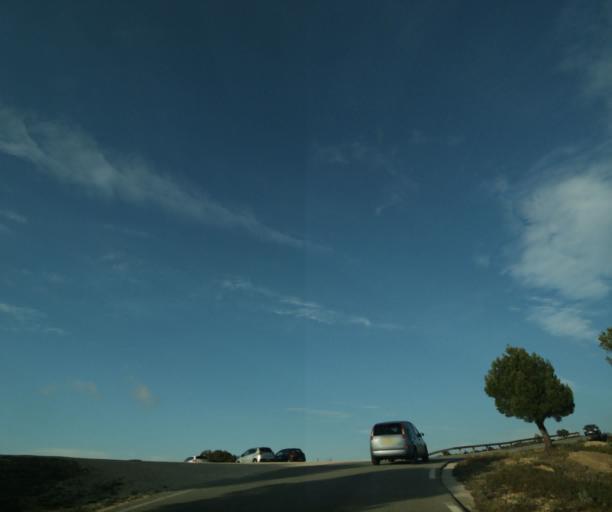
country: FR
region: Provence-Alpes-Cote d'Azur
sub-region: Departement des Bouches-du-Rhone
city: Cassis
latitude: 43.1990
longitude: 5.5533
